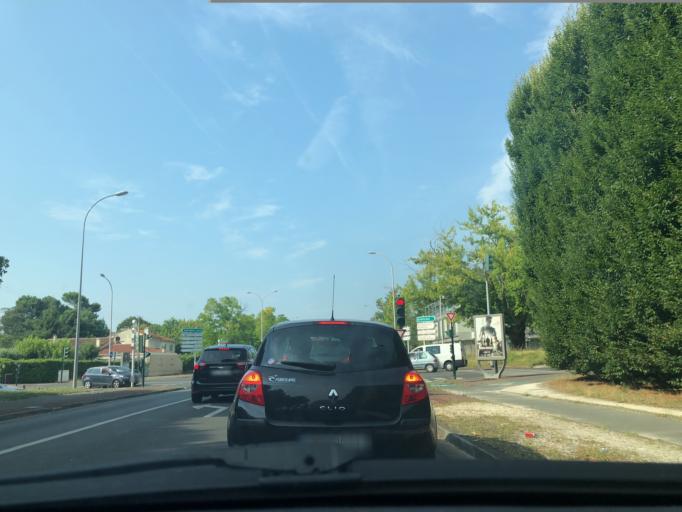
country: FR
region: Aquitaine
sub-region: Departement de la Gironde
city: Merignac
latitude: 44.8398
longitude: -0.6399
